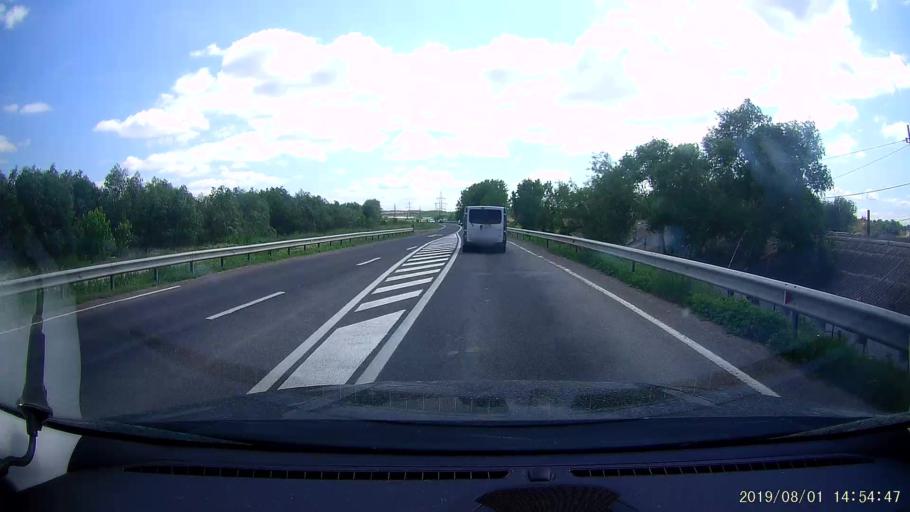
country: RO
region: Braila
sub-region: Municipiul Braila
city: Braila
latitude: 45.3134
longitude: 27.9840
